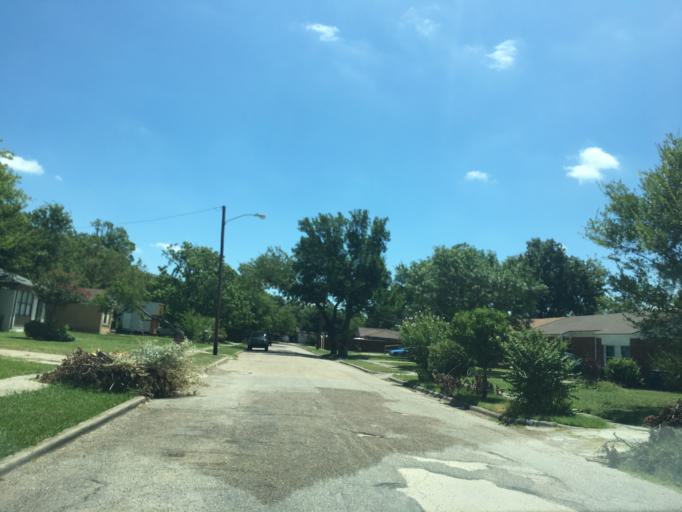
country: US
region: Texas
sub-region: Dallas County
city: Garland
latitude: 32.8420
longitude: -96.6819
